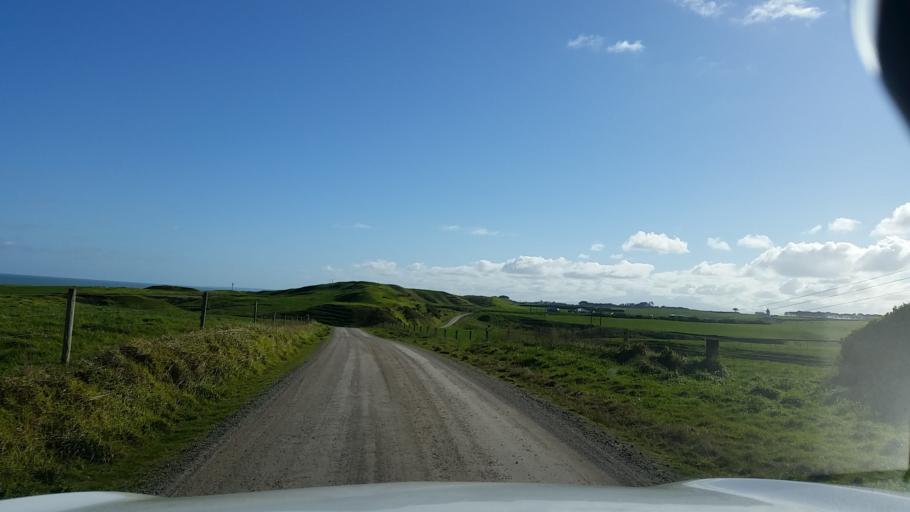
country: NZ
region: Taranaki
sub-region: South Taranaki District
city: Patea
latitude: -39.6860
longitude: 174.3949
